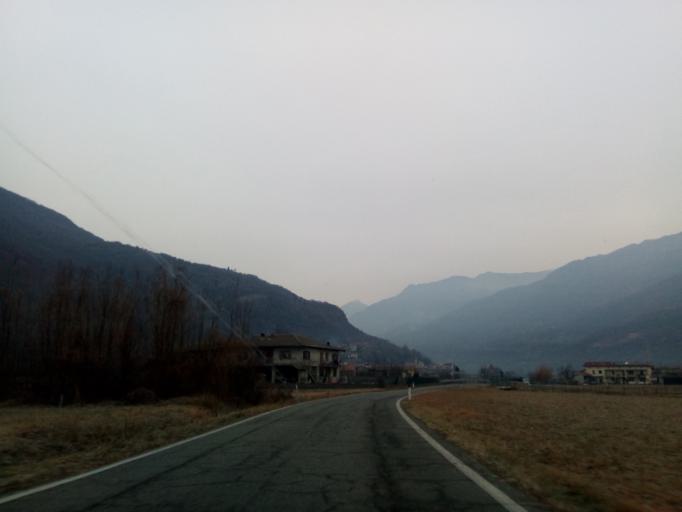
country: IT
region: Piedmont
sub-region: Provincia di Torino
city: Quassolo
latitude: 45.5164
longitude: 7.8328
